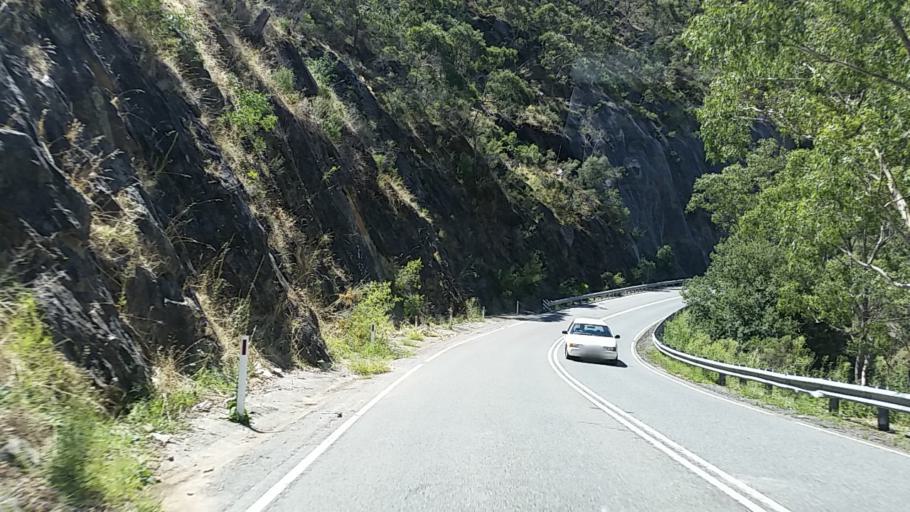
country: AU
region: South Australia
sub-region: Campbelltown
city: Athelstone
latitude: -34.8630
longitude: 138.7635
